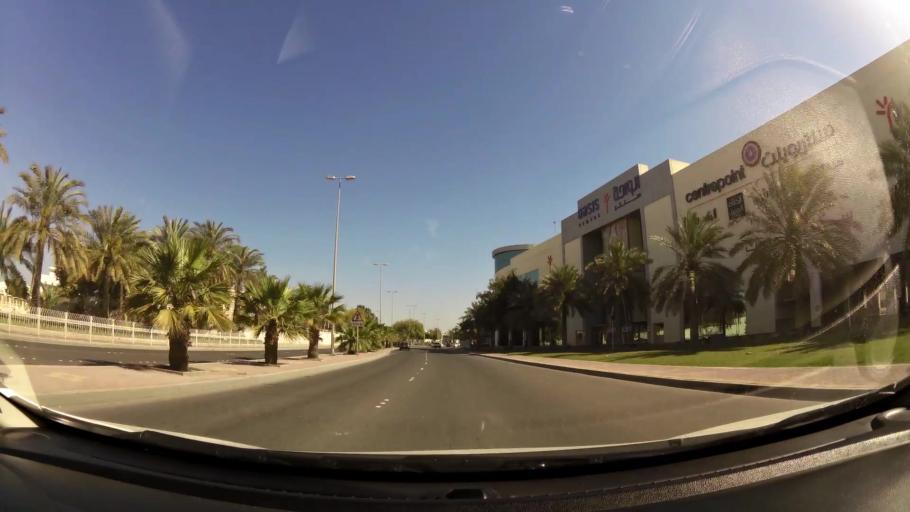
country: BH
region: Muharraq
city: Al Muharraq
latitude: 26.2640
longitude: 50.6154
